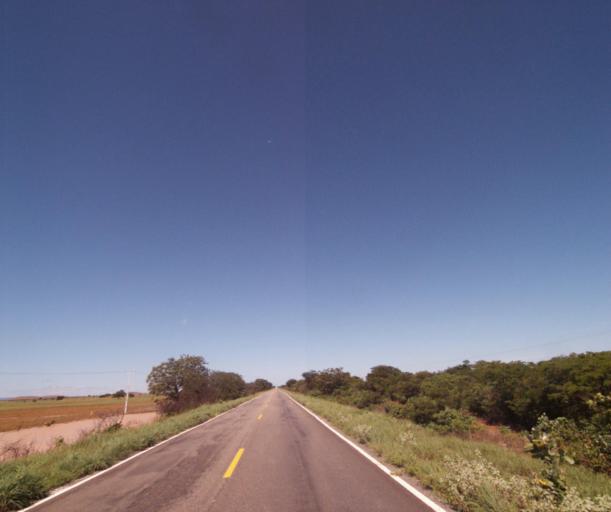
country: BR
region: Bahia
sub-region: Palmas De Monte Alto
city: Palmas de Monte Alto
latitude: -14.2667
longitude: -43.3719
